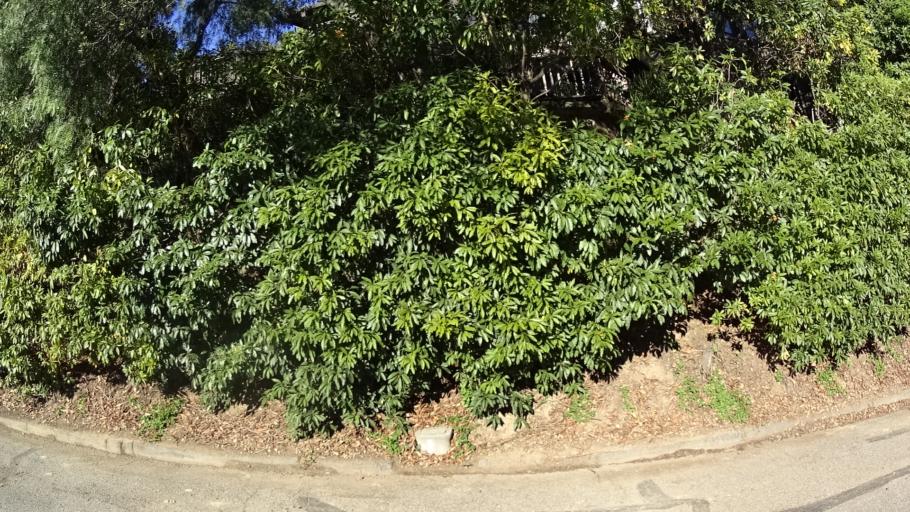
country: US
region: California
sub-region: Alameda County
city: Piedmont
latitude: 37.8314
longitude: -122.2277
